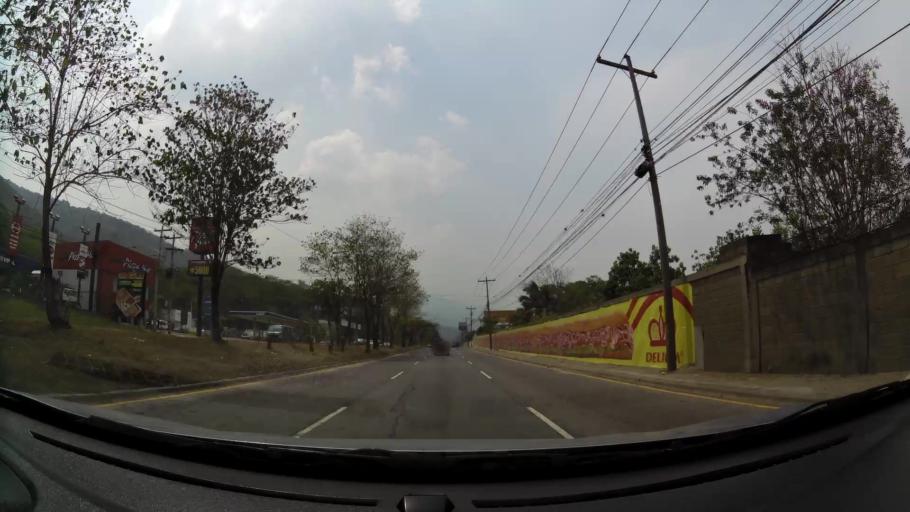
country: HN
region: Cortes
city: San Pedro Sula
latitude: 15.4555
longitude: -88.0249
